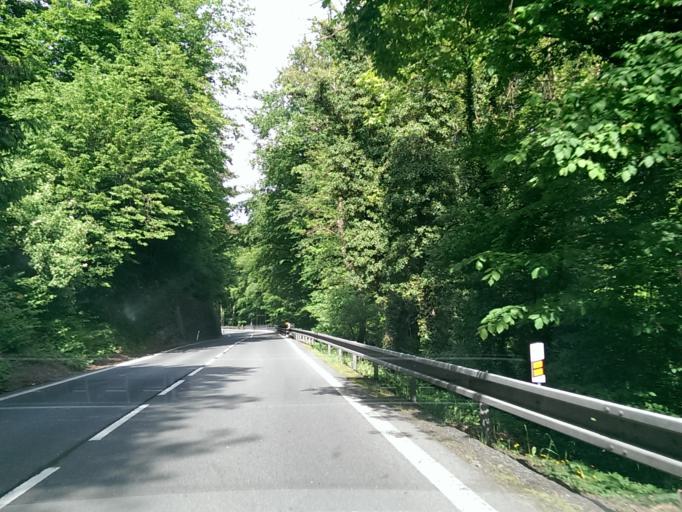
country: CZ
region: Liberecky
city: Mala Skala
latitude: 50.6213
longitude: 15.1734
